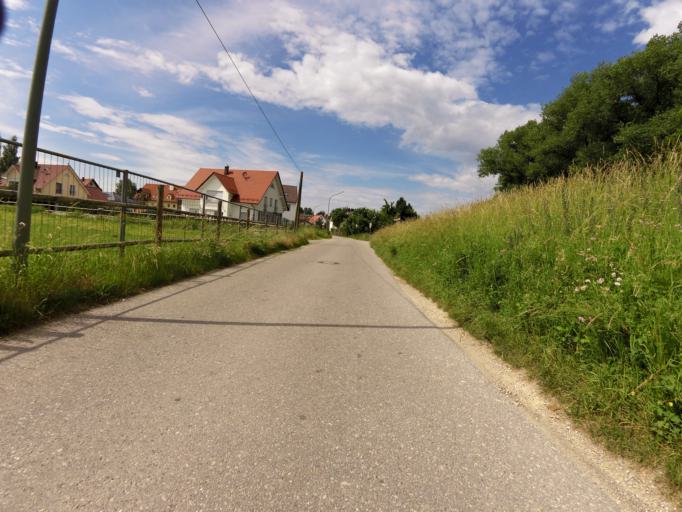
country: DE
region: Bavaria
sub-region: Upper Bavaria
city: Moosburg
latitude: 48.4628
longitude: 11.9442
